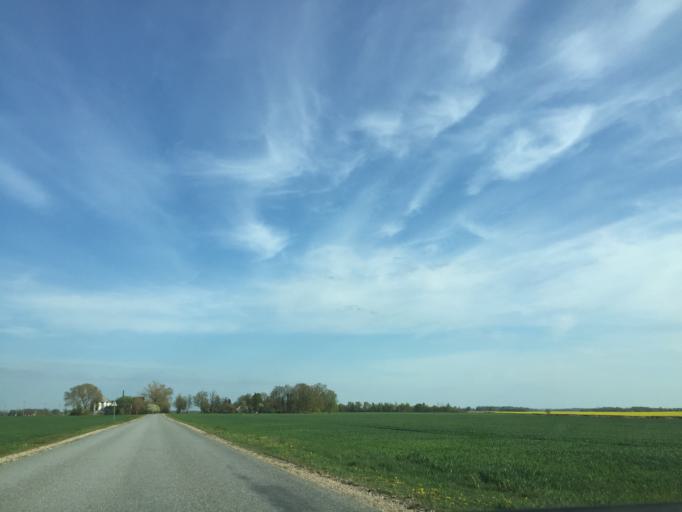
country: LV
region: Bauskas Rajons
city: Bauska
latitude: 56.3773
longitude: 24.2182
